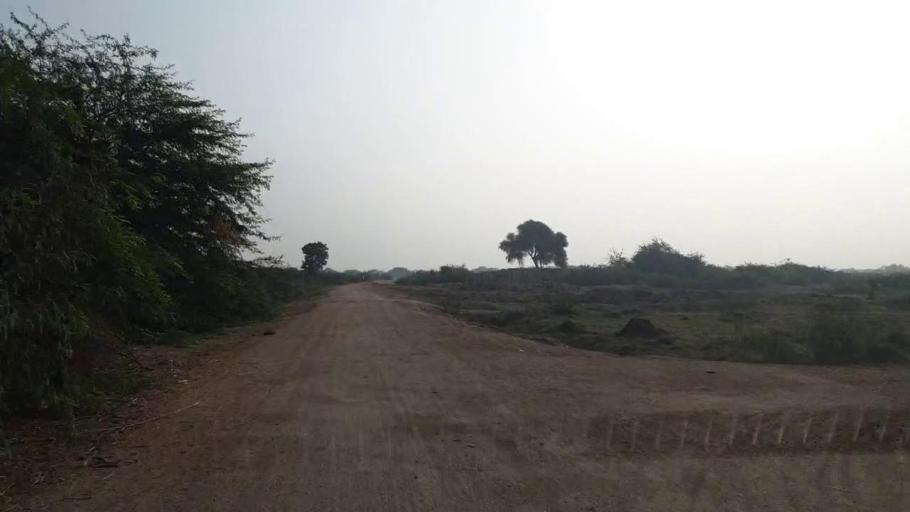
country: PK
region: Sindh
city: Tando Muhammad Khan
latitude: 25.1615
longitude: 68.5913
